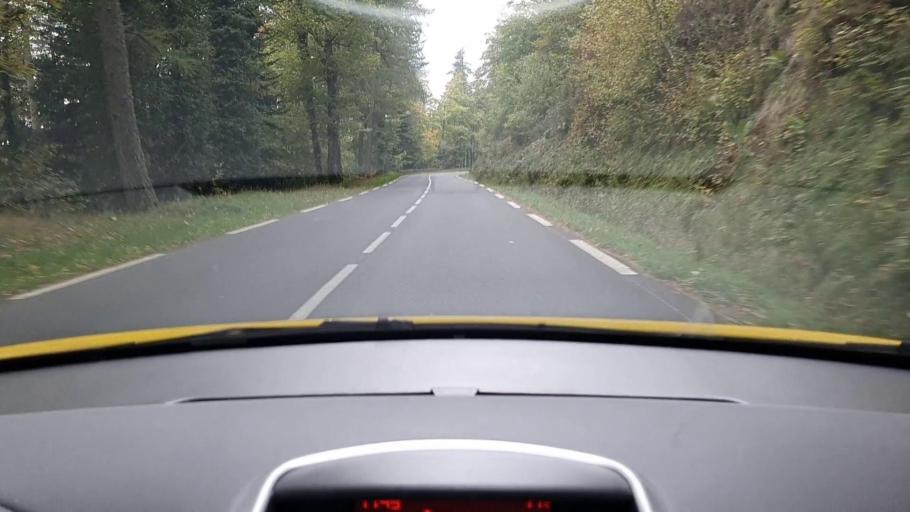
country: FR
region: Languedoc-Roussillon
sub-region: Departement de la Lozere
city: Meyrueis
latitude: 44.1334
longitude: 3.4260
